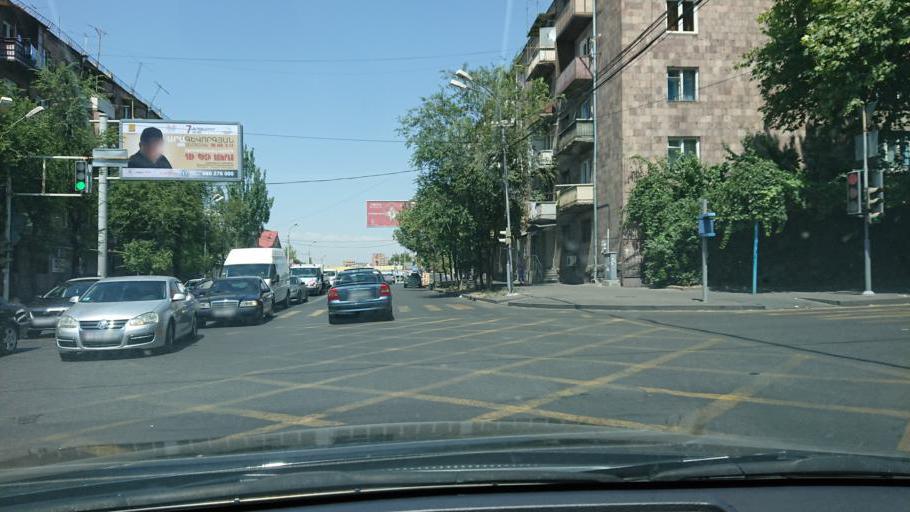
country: AM
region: Yerevan
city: Yerevan
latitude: 40.2049
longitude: 44.4973
